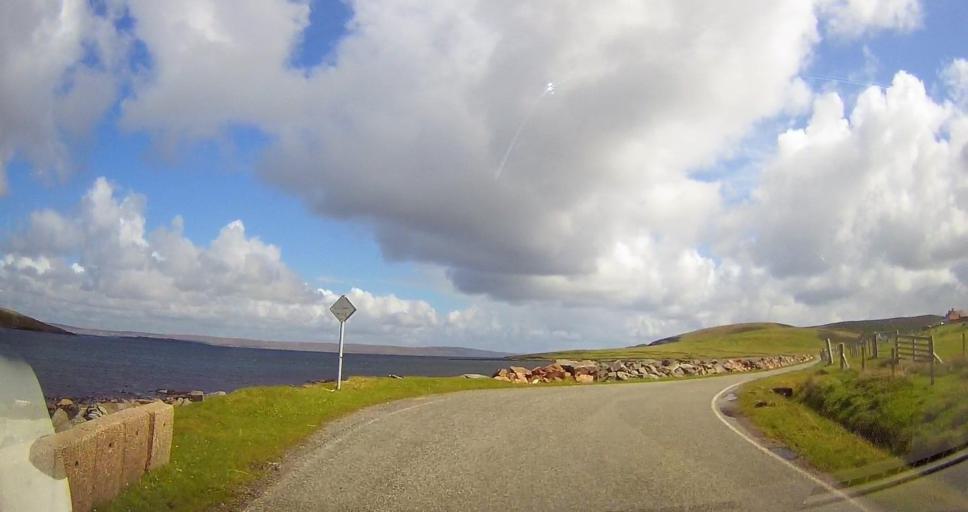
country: GB
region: Scotland
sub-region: Shetland Islands
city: Lerwick
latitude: 60.5811
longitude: -1.3347
